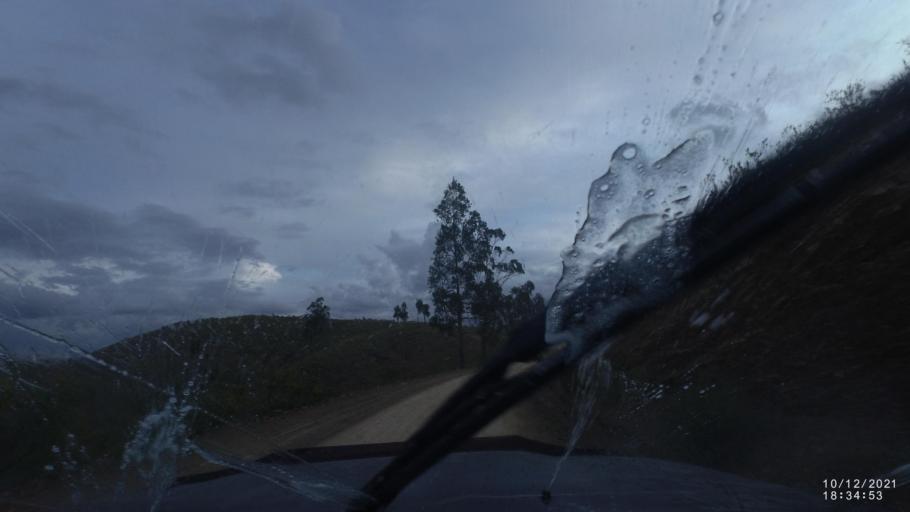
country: BO
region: Cochabamba
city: Tarata
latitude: -17.8243
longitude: -65.9901
